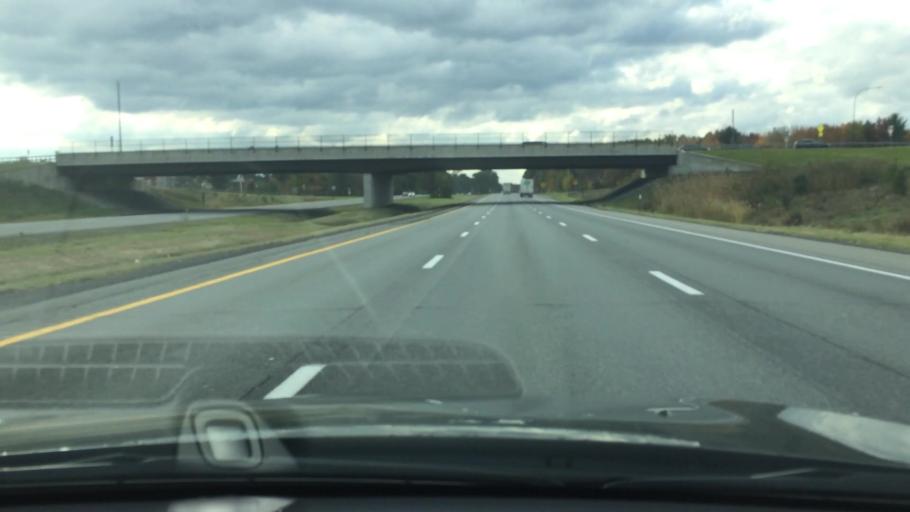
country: US
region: New York
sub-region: Saratoga County
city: Ballston Spa
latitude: 42.9714
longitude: -73.8022
